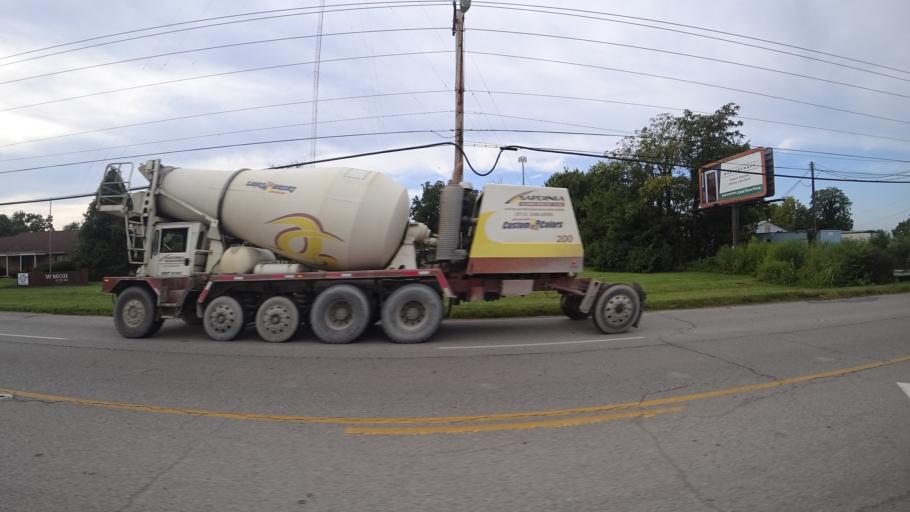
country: US
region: Ohio
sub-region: Butler County
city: Hamilton
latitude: 39.4038
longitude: -84.5307
